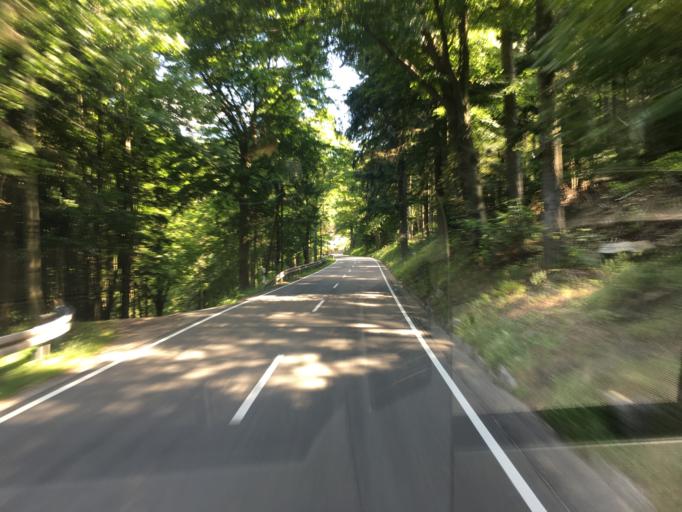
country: DE
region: Baden-Wuerttemberg
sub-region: Freiburg Region
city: Seebach
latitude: 48.5829
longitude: 8.2045
